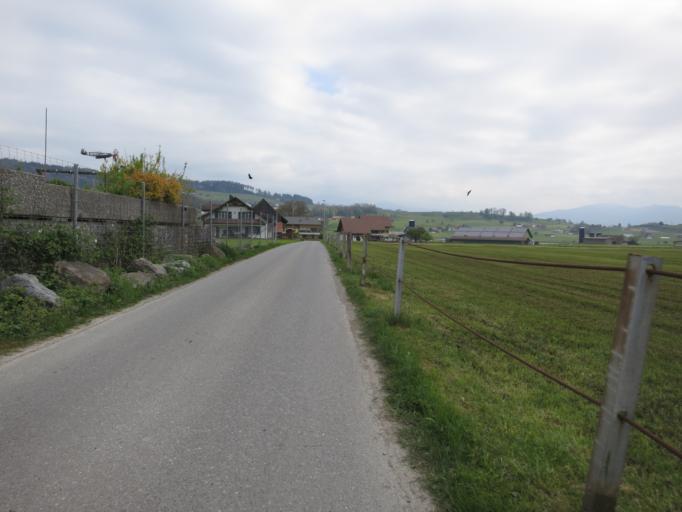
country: CH
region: Schwyz
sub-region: Bezirk March
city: Schubelbach
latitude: 47.1835
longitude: 8.9102
